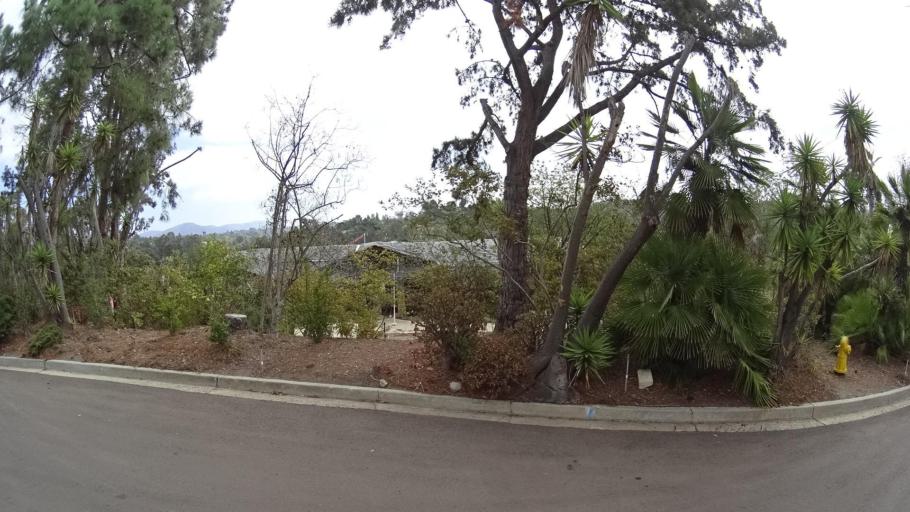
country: US
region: California
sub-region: San Diego County
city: Rancho Santa Fe
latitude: 33.0209
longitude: -117.2322
